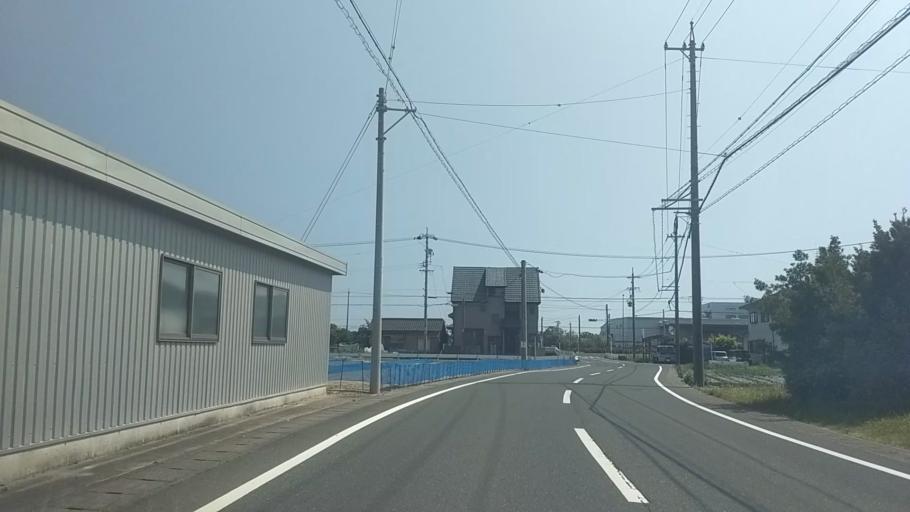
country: JP
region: Shizuoka
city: Hamamatsu
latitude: 34.6721
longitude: 137.7159
